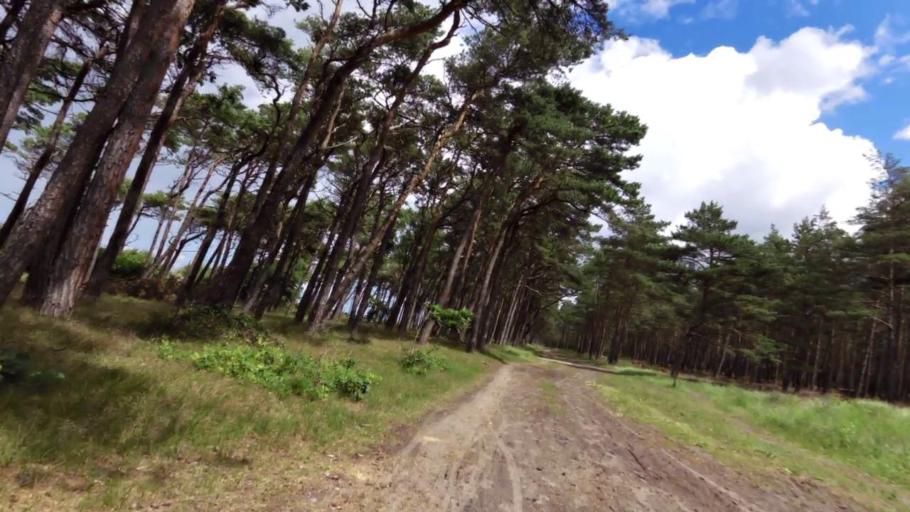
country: PL
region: West Pomeranian Voivodeship
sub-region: Powiat slawienski
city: Darlowo
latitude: 54.4965
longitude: 16.4484
